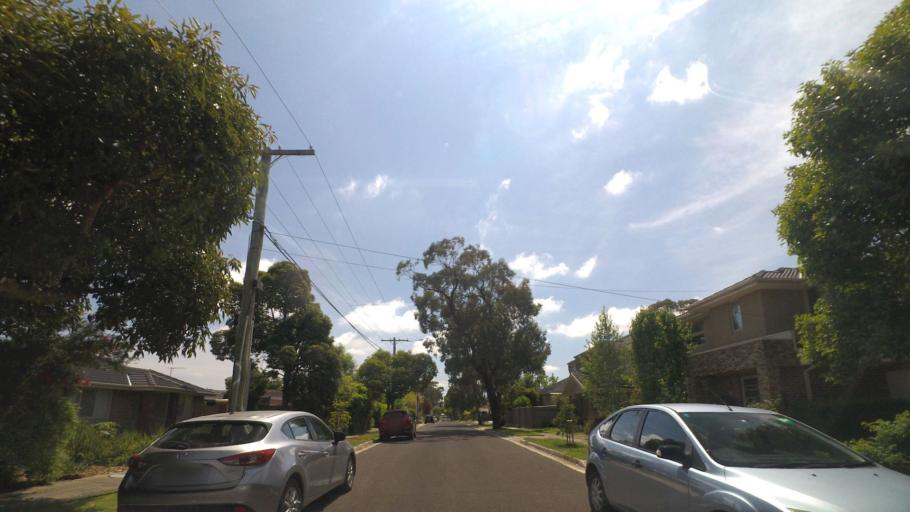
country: AU
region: Victoria
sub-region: Knox
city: Bayswater
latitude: -37.8466
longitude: 145.2588
